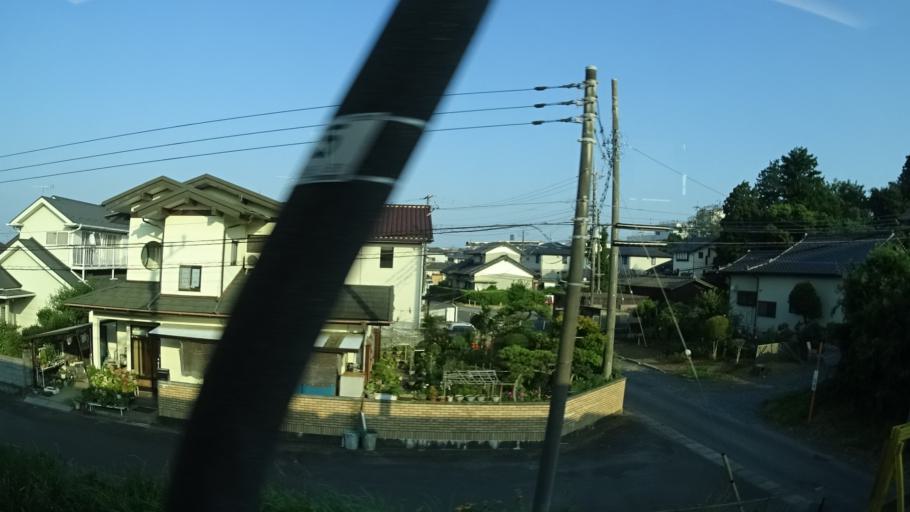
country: JP
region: Ibaraki
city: Funaishikawa
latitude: 36.4700
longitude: 140.5718
